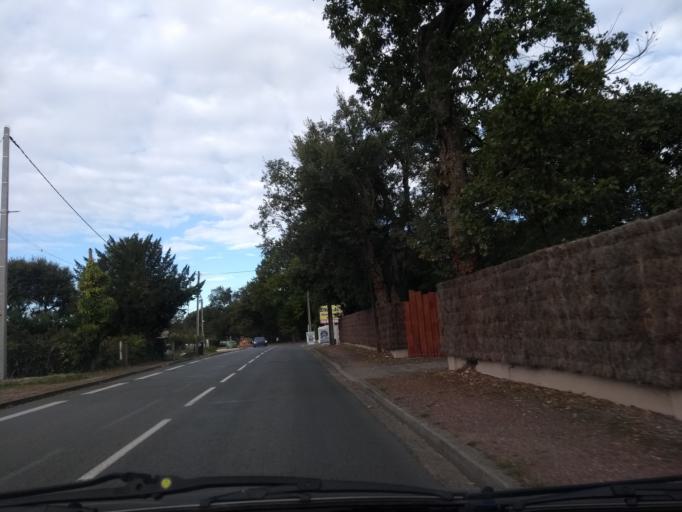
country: FR
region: Aquitaine
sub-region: Departement de la Gironde
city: Canejan
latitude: 44.7736
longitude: -0.6352
